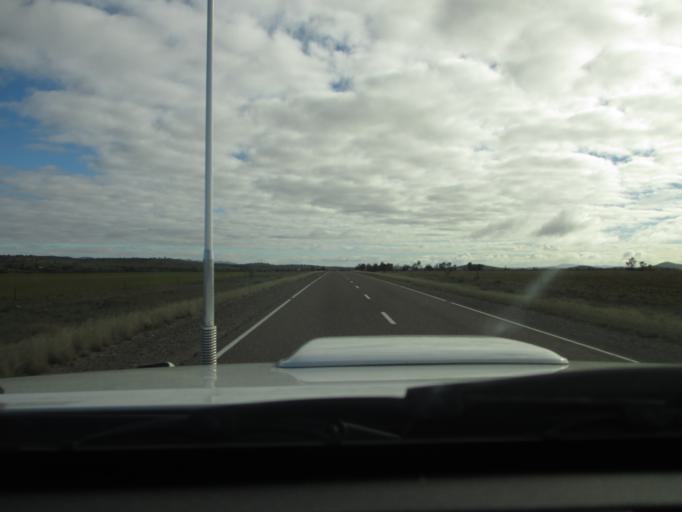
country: AU
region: South Australia
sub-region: Peterborough
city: Peterborough
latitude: -32.5378
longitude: 138.5575
